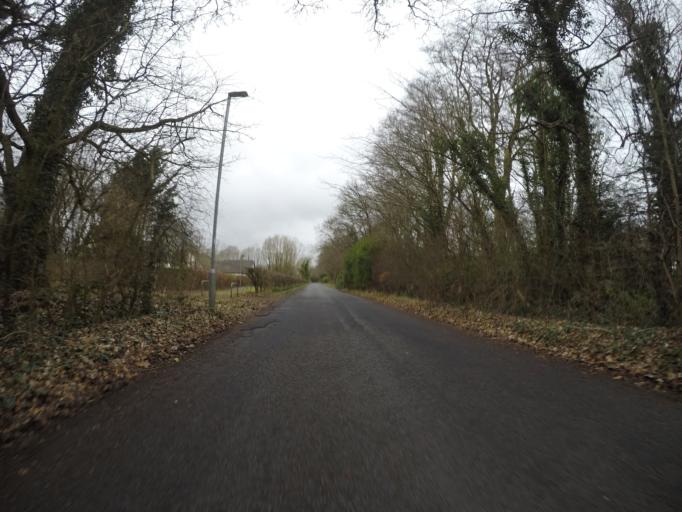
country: GB
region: Scotland
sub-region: North Ayrshire
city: Springside
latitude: 55.6276
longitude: -4.6159
